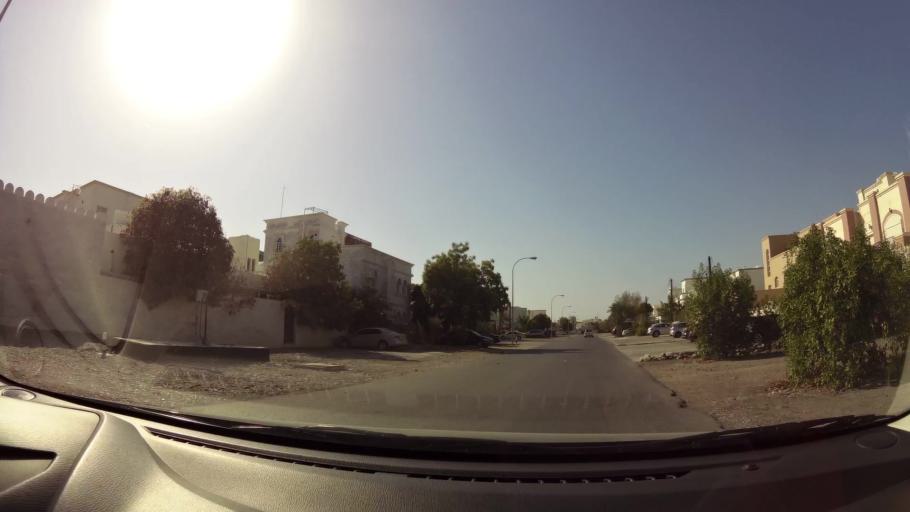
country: OM
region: Muhafazat Masqat
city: As Sib al Jadidah
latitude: 23.6275
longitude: 58.2041
